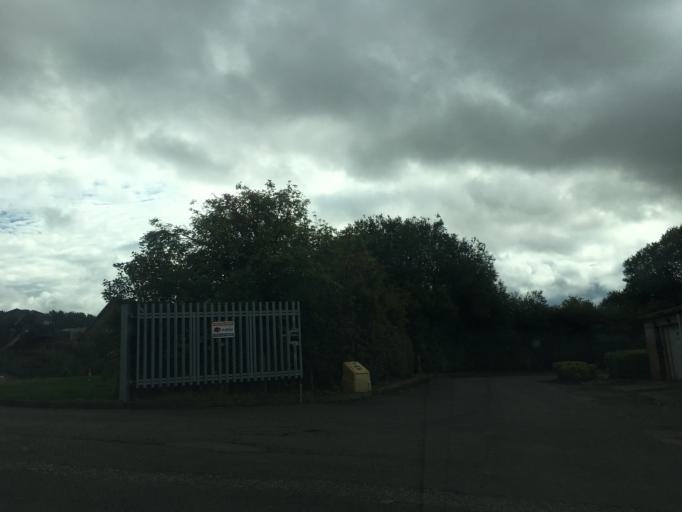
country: GB
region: Scotland
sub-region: Midlothian
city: Gorebridge
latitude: 55.8656
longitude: -3.0511
